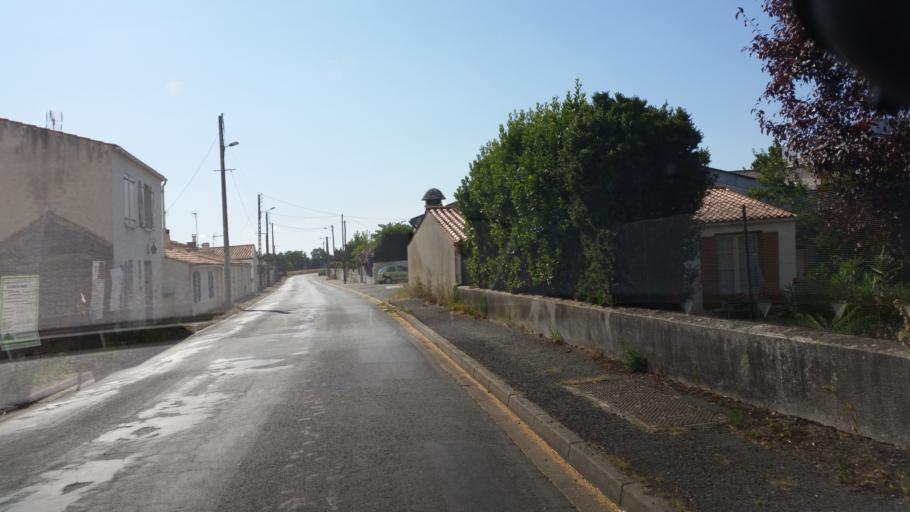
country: FR
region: Poitou-Charentes
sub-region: Departement de la Charente-Maritime
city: Marans
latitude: 46.3049
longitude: -1.0013
